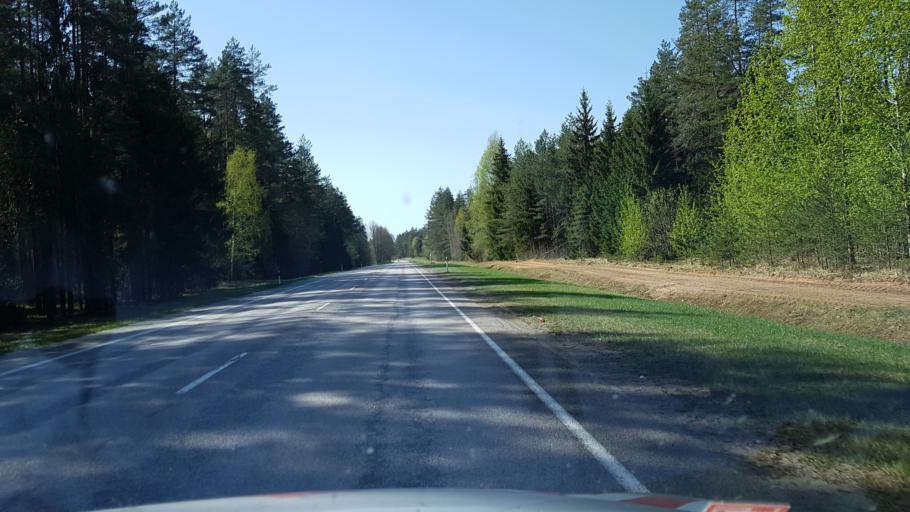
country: EE
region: Valgamaa
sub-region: Valga linn
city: Valga
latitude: 57.8203
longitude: 26.0483
